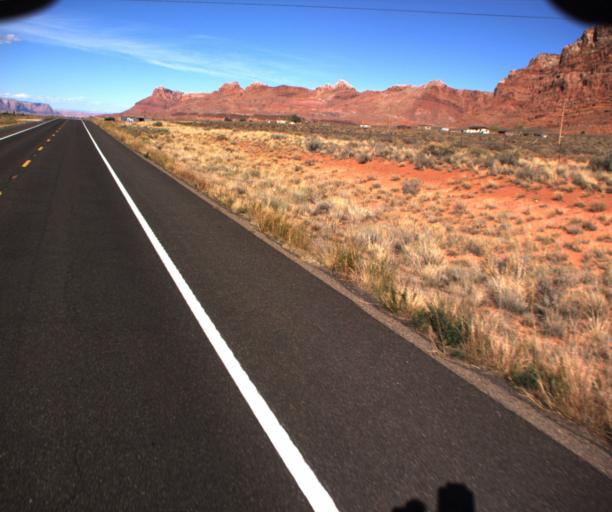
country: US
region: Arizona
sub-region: Coconino County
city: LeChee
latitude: 36.6141
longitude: -111.6547
